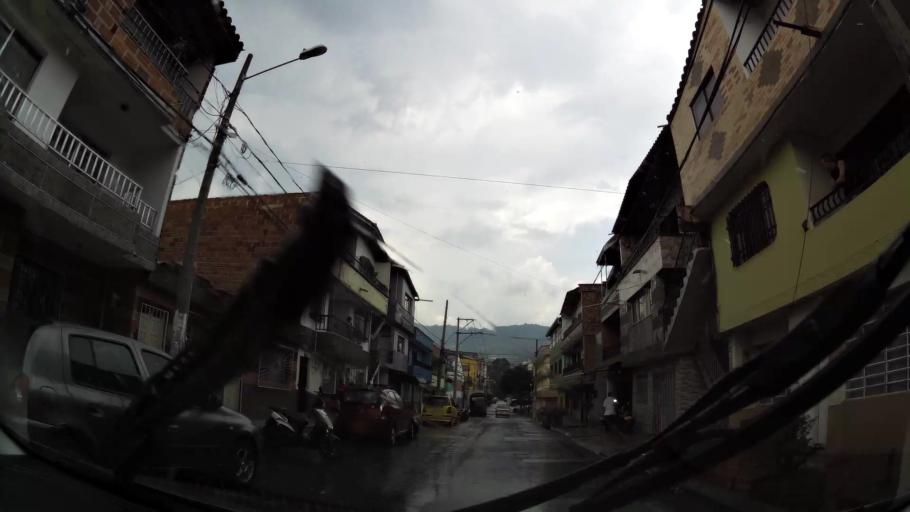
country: CO
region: Antioquia
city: Itagui
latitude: 6.1795
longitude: -75.5982
